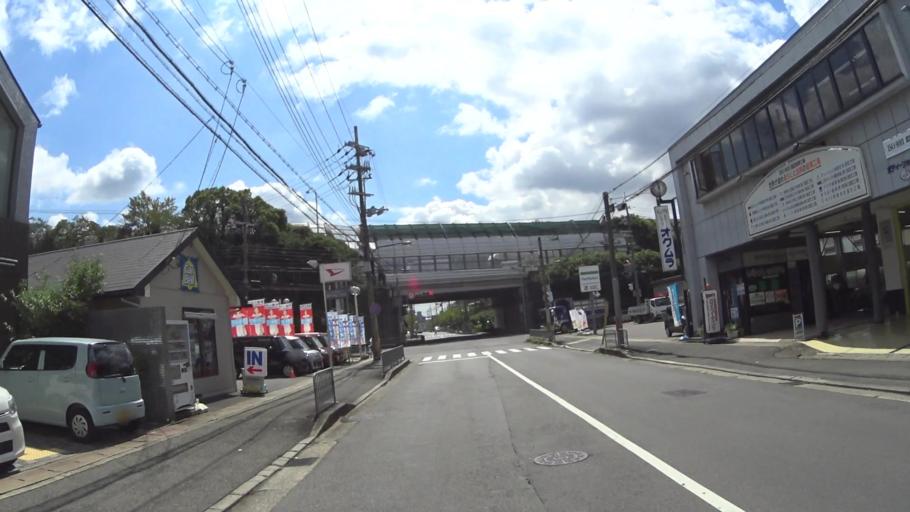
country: JP
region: Shiga Prefecture
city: Otsu-shi
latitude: 34.9638
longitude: 135.8087
